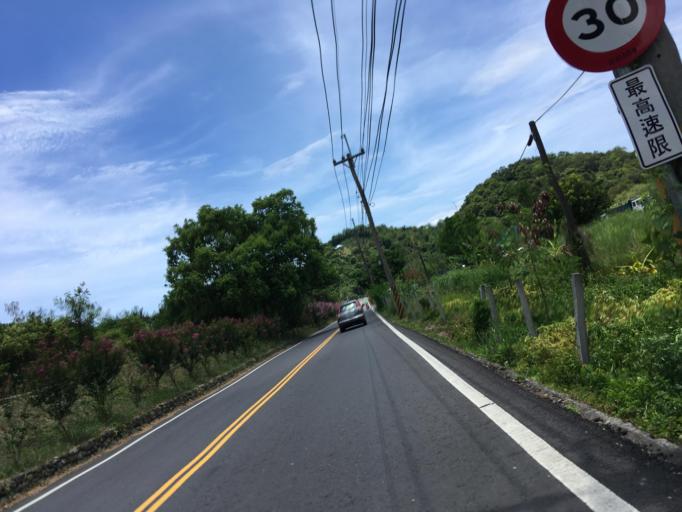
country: TW
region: Taiwan
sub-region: Yilan
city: Yilan
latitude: 24.6412
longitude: 121.7195
